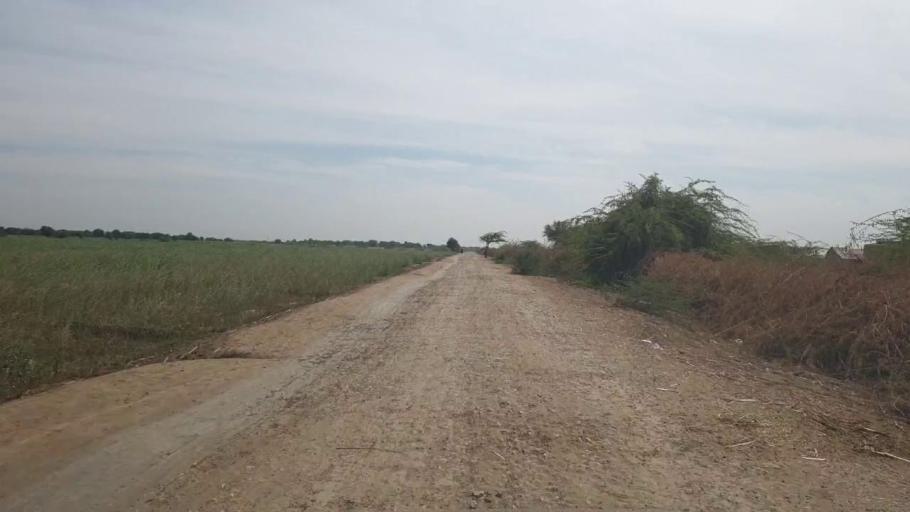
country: PK
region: Sindh
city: Kunri
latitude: 25.3021
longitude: 69.5758
